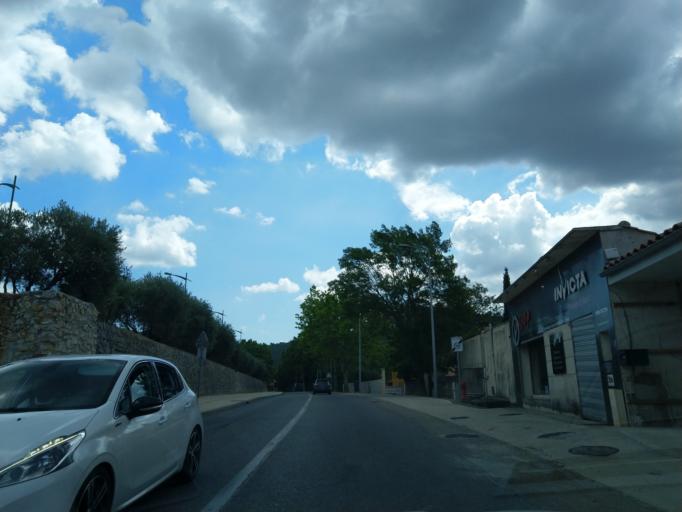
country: FR
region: Provence-Alpes-Cote d'Azur
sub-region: Departement du Var
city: Saint-Zacharie
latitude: 43.3854
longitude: 5.7123
